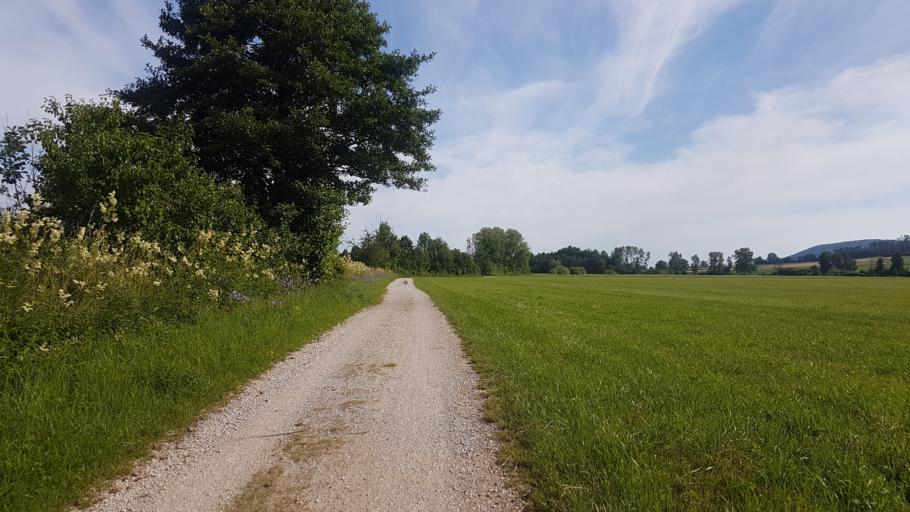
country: DE
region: Bavaria
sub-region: Regierungsbezirk Mittelfranken
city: Treuchtlingen
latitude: 48.9685
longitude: 10.9126
